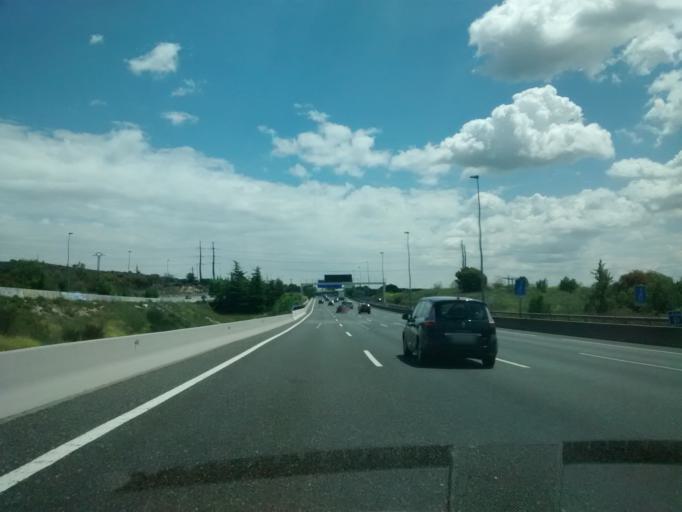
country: ES
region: Madrid
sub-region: Provincia de Madrid
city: Collado-Villalba
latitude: 40.6197
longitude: -3.9861
